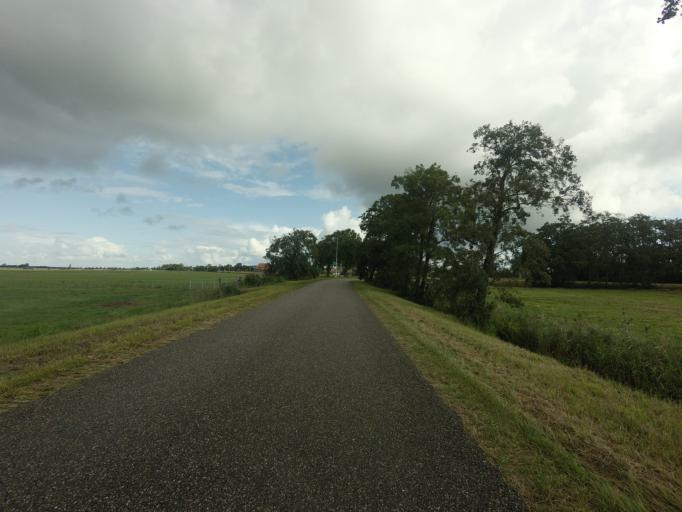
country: NL
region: Friesland
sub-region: Gemeente Tytsjerksteradiel
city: Garyp
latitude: 53.1539
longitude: 5.9507
